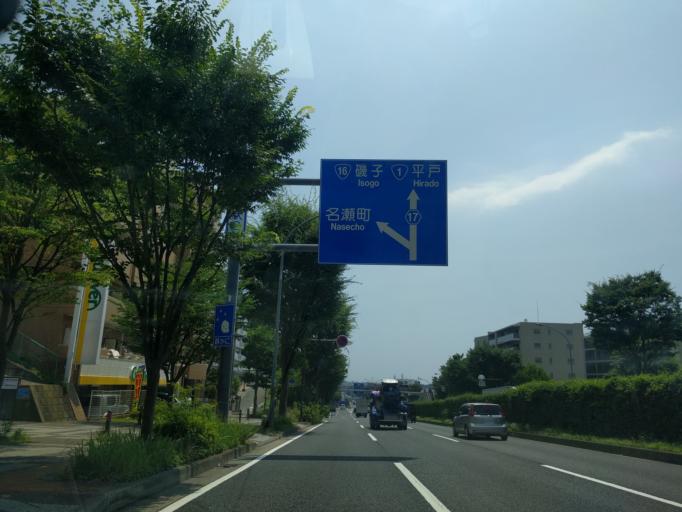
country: JP
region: Kanagawa
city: Yokohama
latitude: 35.4294
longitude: 139.5623
